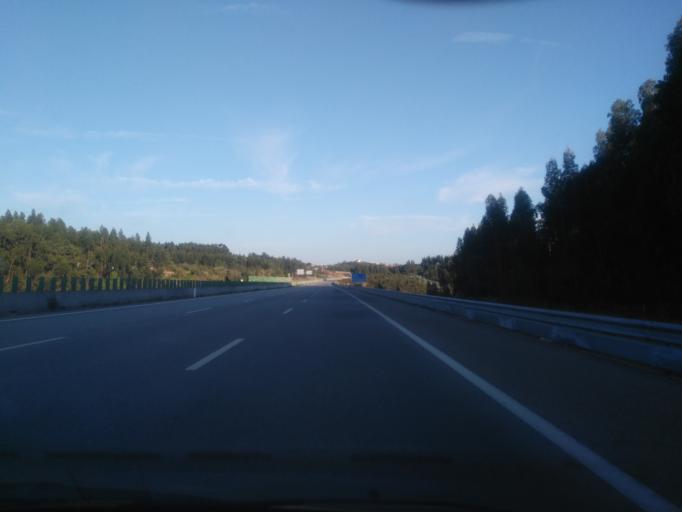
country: PT
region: Coimbra
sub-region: Figueira da Foz
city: Alhadas
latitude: 40.1522
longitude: -8.7662
